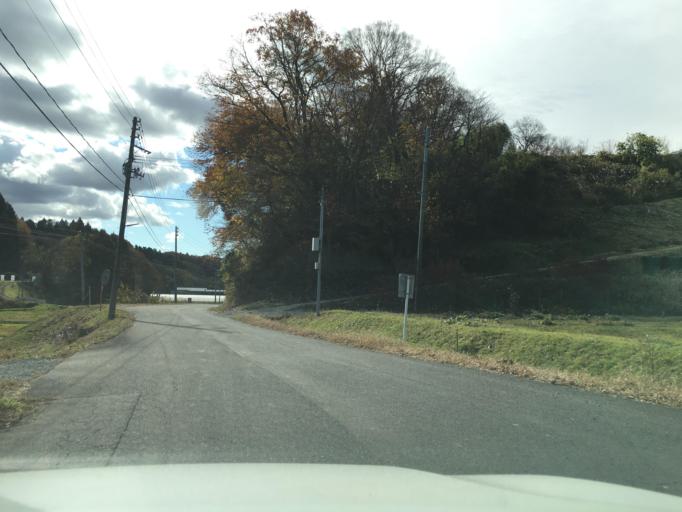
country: JP
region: Fukushima
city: Miharu
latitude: 37.5056
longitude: 140.4903
